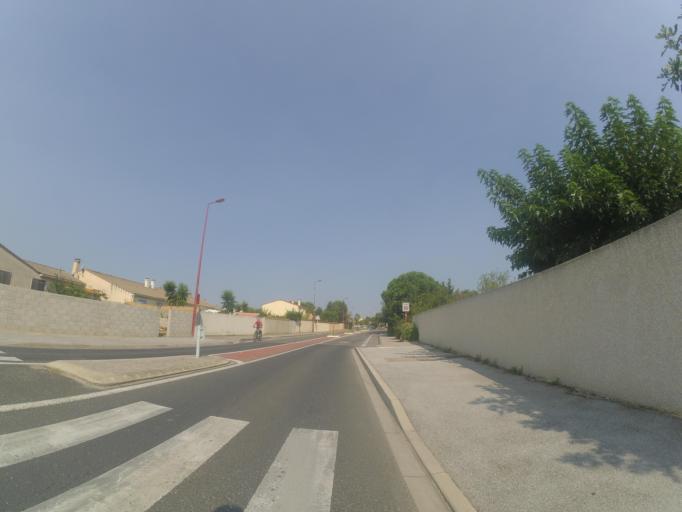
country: FR
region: Languedoc-Roussillon
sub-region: Departement des Pyrenees-Orientales
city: Toulouges
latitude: 42.6674
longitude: 2.8381
